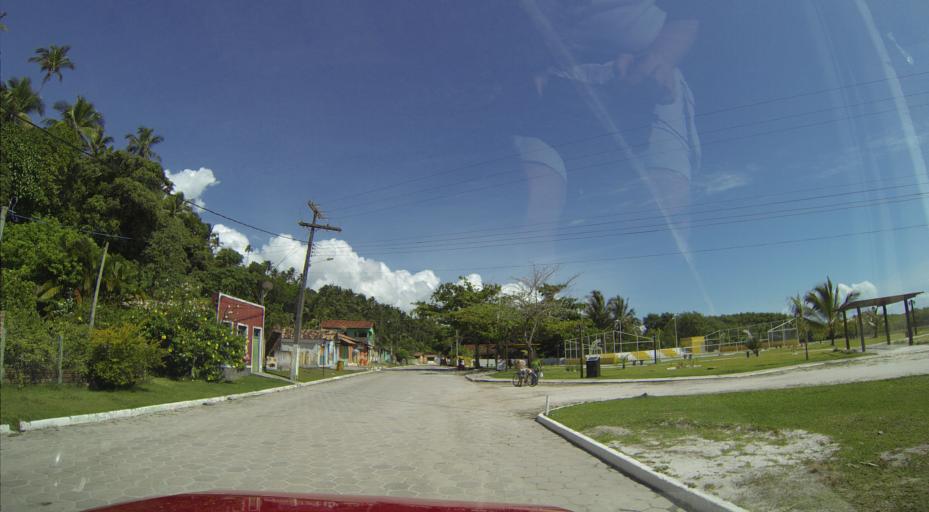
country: BR
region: Bahia
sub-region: Santa Cruz Cabralia
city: Santa Cruz Cabralia
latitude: -16.0865
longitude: -38.9527
